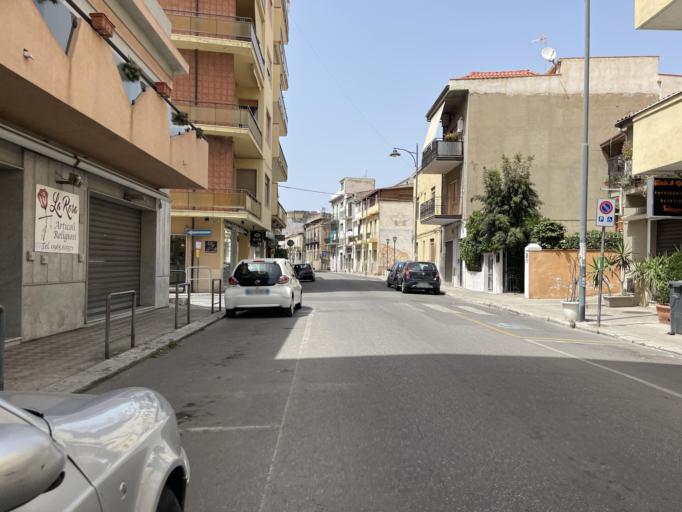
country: IT
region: Calabria
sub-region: Provincia di Reggio Calabria
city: Reggio Calabria
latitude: 38.0963
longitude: 15.6433
